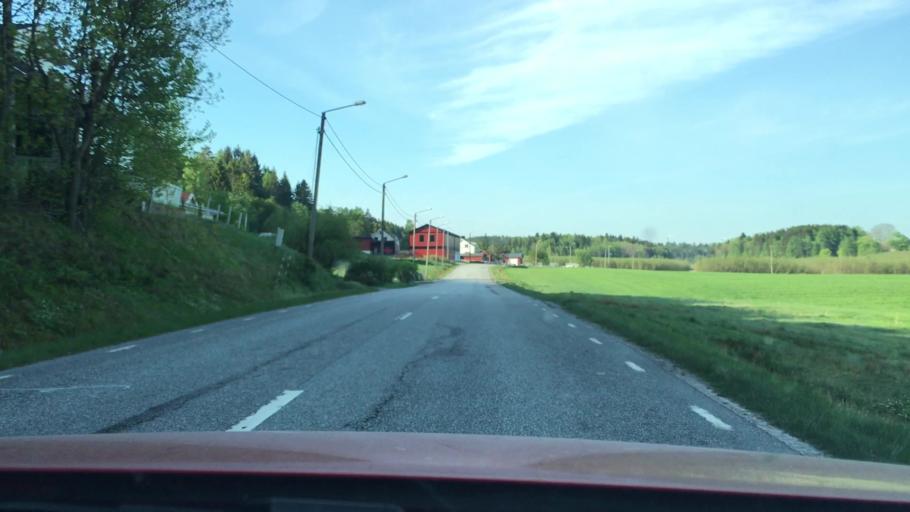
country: SE
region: Vaestra Goetaland
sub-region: Munkedals Kommun
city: Munkedal
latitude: 58.6025
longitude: 11.5572
